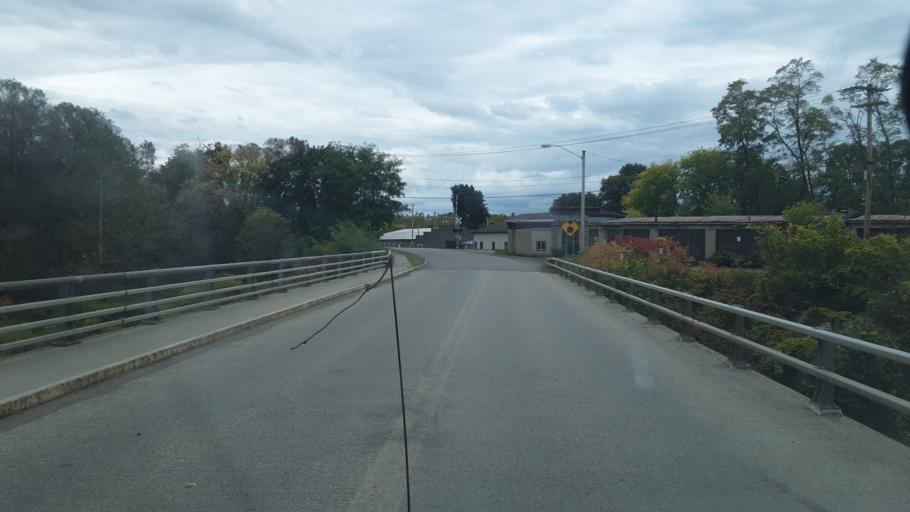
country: US
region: New York
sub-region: Allegany County
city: Belmont
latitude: 42.2266
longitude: -78.0319
